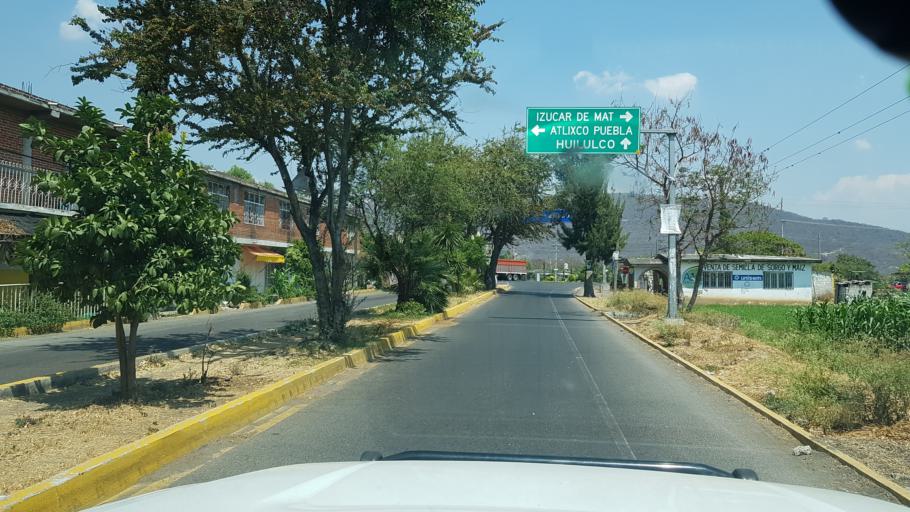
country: MX
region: Puebla
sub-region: Huaquechula
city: Cacaloxuchitl
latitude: 18.7906
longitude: -98.4552
